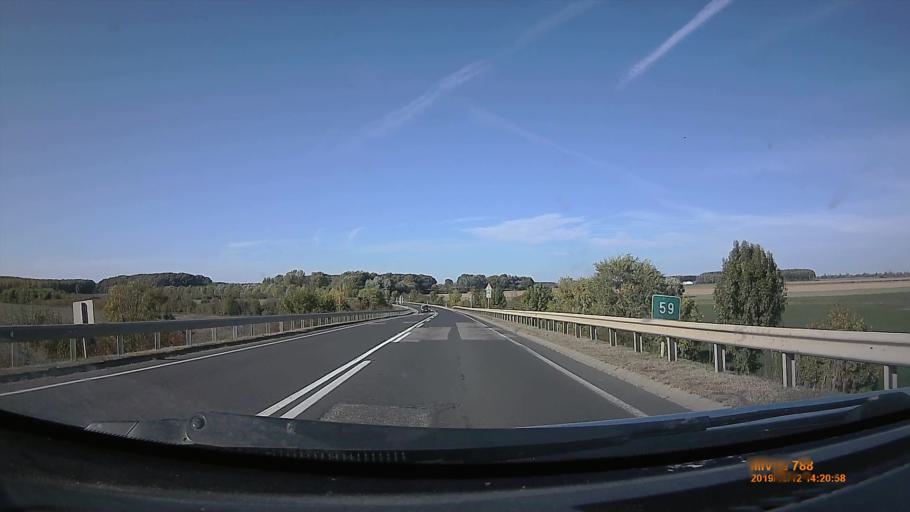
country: HU
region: Hajdu-Bihar
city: Biharkeresztes
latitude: 47.1351
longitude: 21.7404
